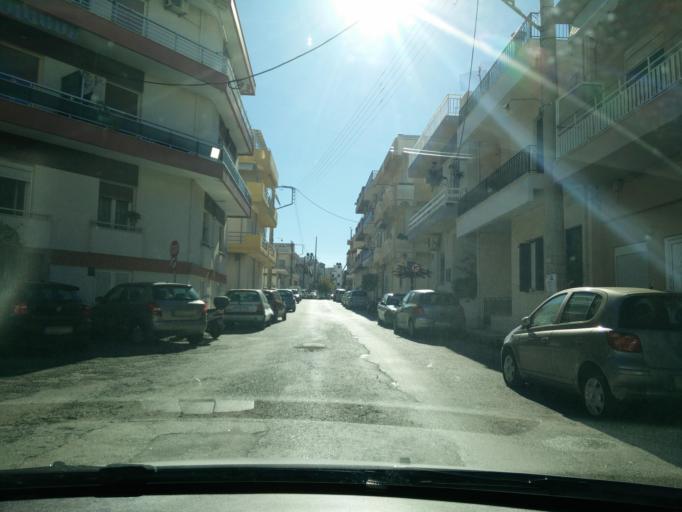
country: GR
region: Crete
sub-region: Nomos Irakleiou
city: Irakleion
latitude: 35.3340
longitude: 25.1456
